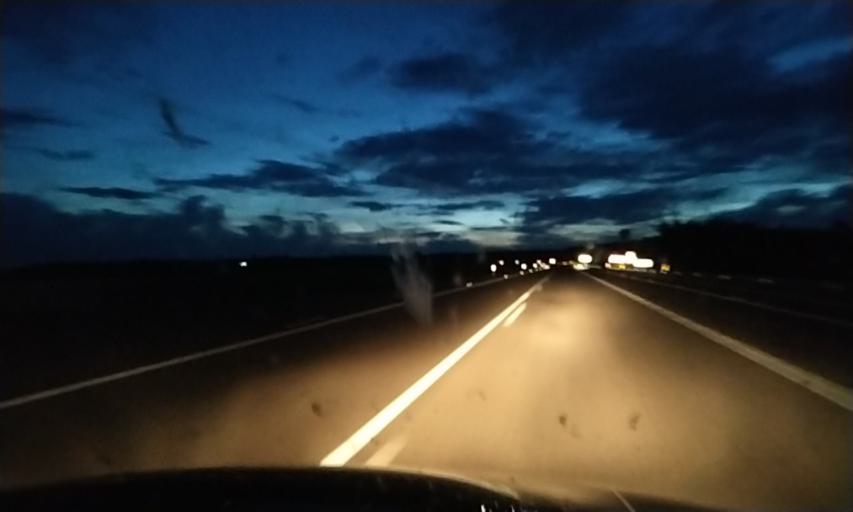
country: ES
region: Extremadura
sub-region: Provincia de Caceres
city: Galisteo
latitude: 39.9848
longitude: -6.2654
